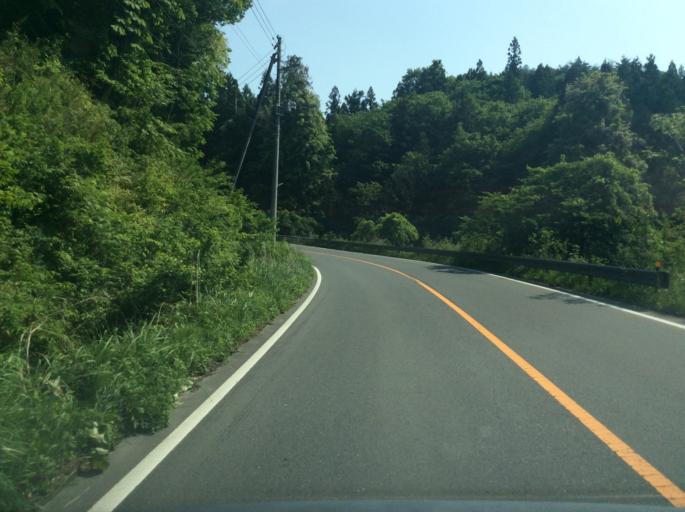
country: JP
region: Tochigi
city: Kuroiso
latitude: 37.0900
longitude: 140.2230
